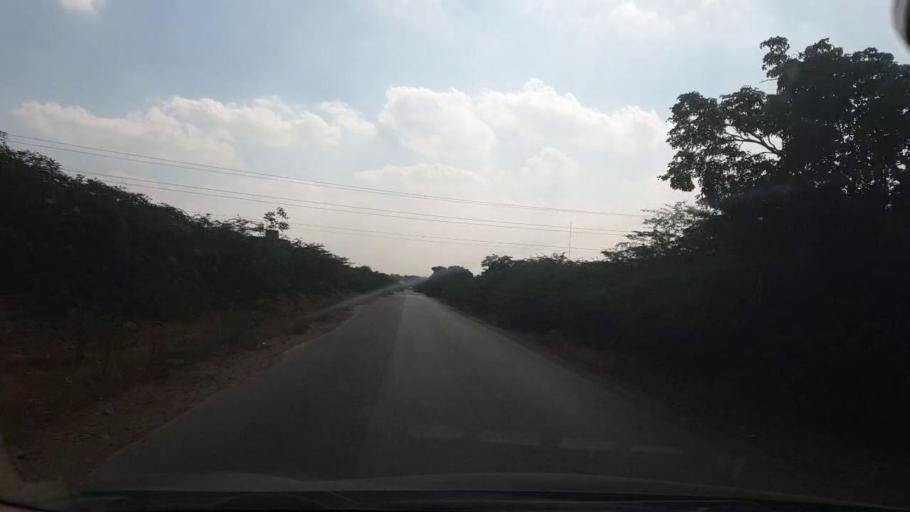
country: PK
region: Sindh
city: Malir Cantonment
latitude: 25.0110
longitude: 67.3543
